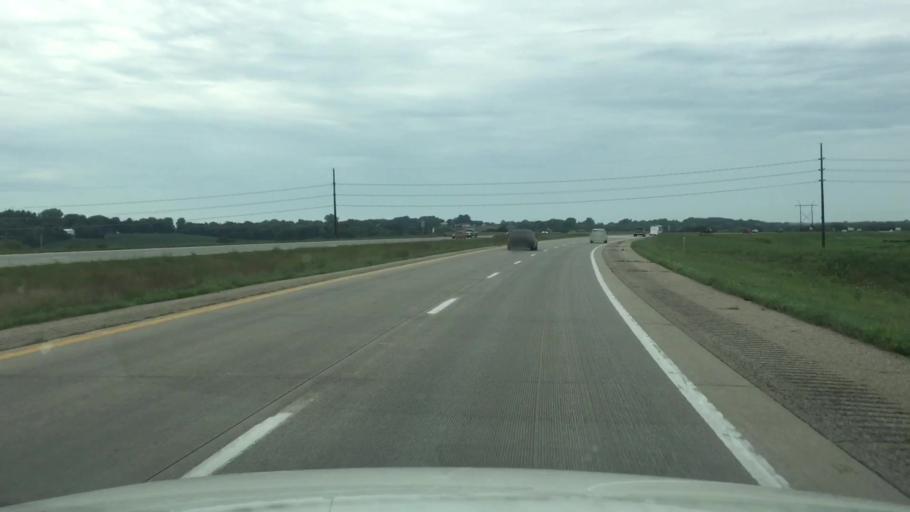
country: US
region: Iowa
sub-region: Warren County
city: Norwalk
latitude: 41.4986
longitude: -93.6232
